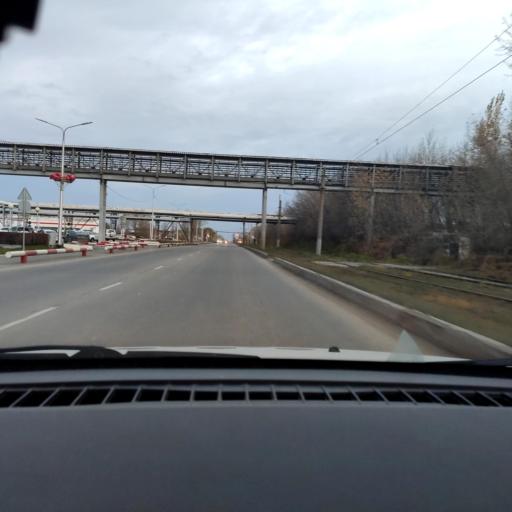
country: RU
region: Perm
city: Kondratovo
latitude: 57.9239
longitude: 56.1394
